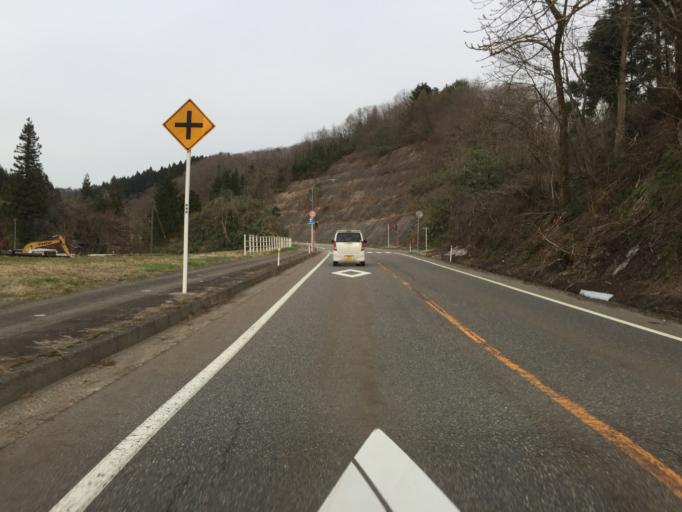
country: JP
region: Niigata
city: Kamo
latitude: 37.6334
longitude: 139.1005
